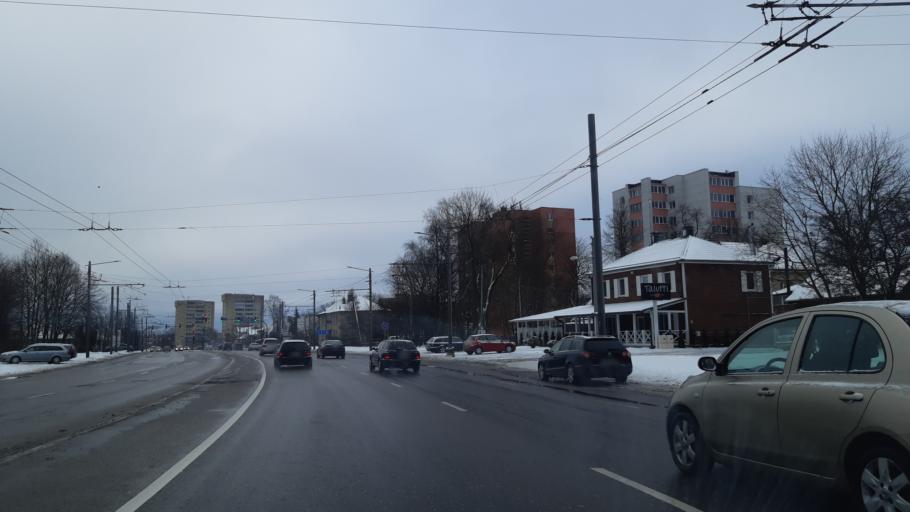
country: LT
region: Kauno apskritis
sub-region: Kaunas
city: Eiguliai
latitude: 54.9114
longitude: 23.9393
